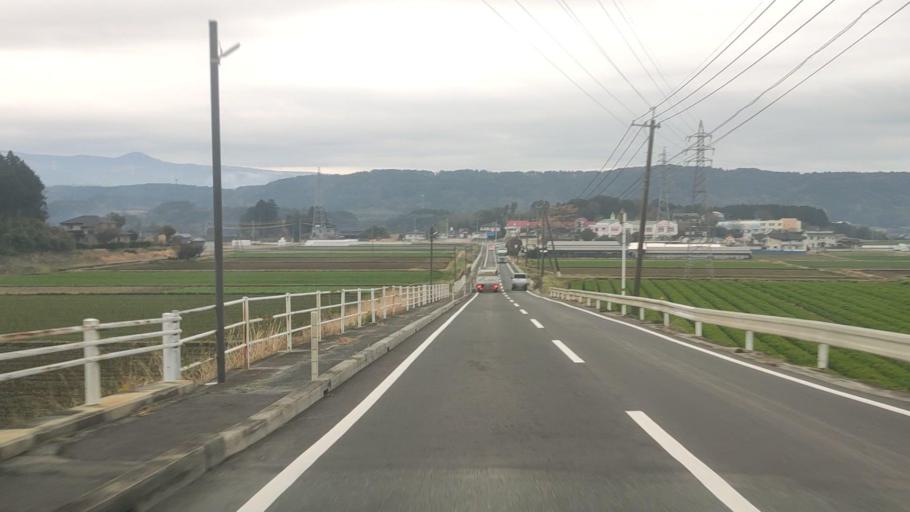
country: JP
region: Kumamoto
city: Ozu
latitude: 32.8689
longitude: 130.8902
